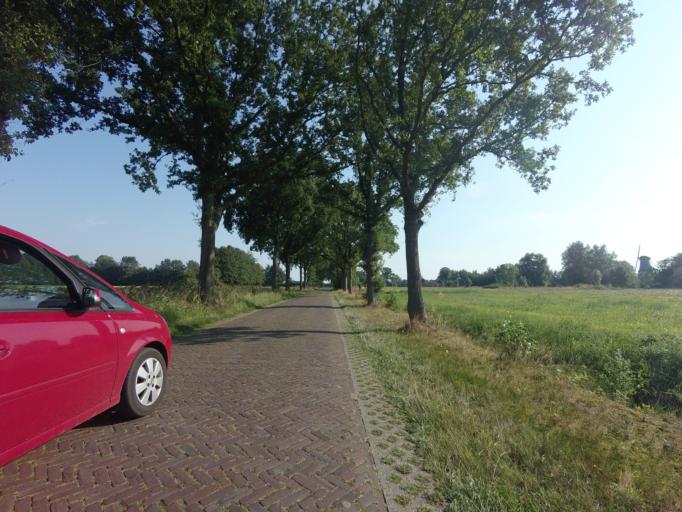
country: NL
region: Groningen
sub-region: Gemeente Zuidhorn
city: Aduard
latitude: 53.1712
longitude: 6.4769
